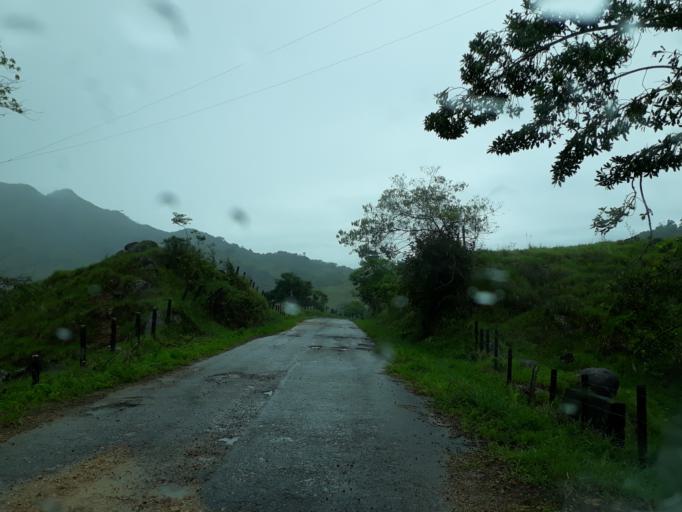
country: CO
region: Cundinamarca
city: Medina
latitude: 4.6736
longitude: -73.3245
